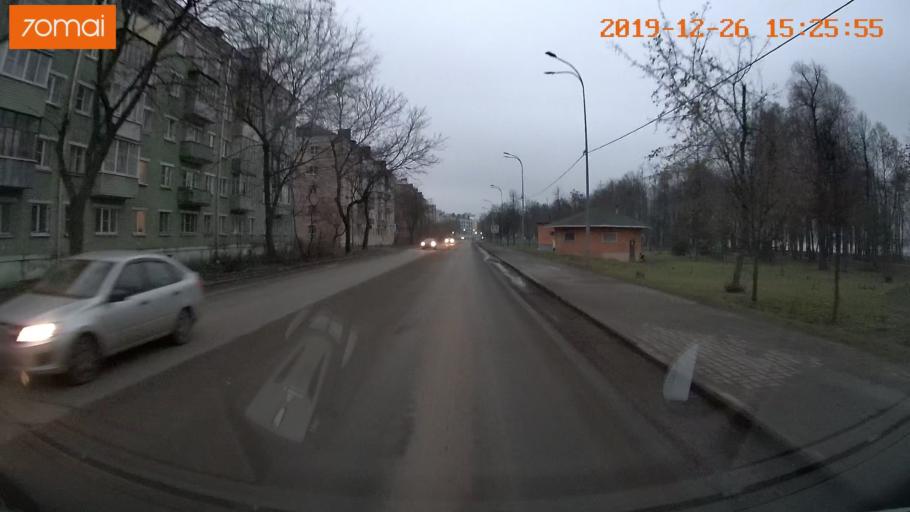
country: RU
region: Jaroslavl
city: Rybinsk
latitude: 58.0552
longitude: 38.8336
